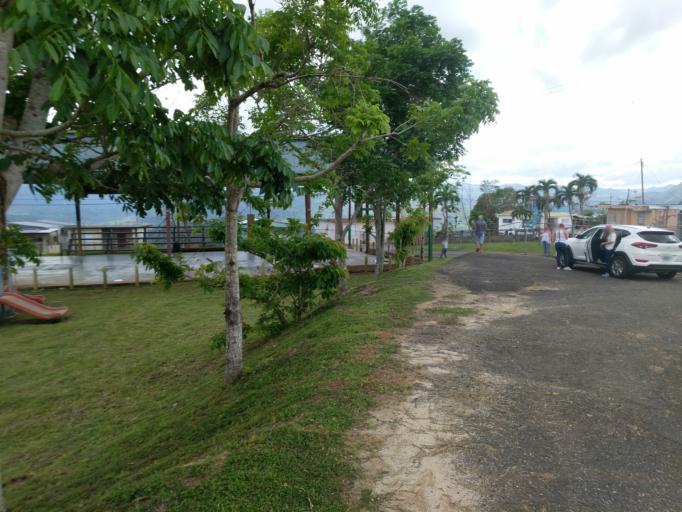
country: PR
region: Utuado
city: Cayuco
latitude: 18.2856
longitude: -66.7216
